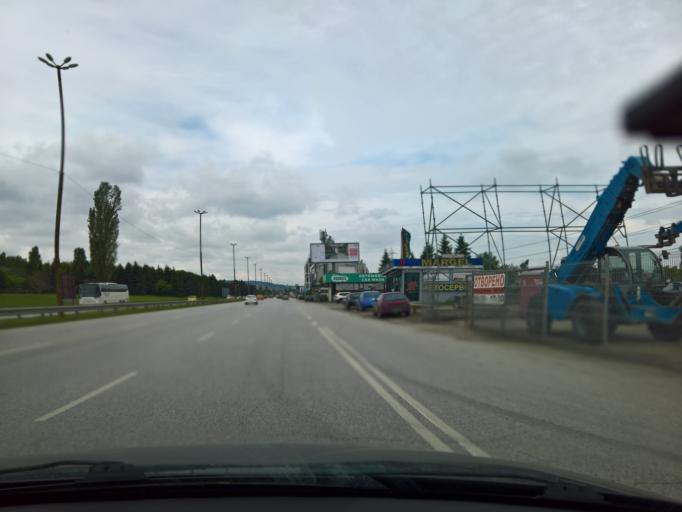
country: BG
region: Sofia-Capital
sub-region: Stolichna Obshtina
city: Sofia
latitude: 42.6560
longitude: 23.2770
